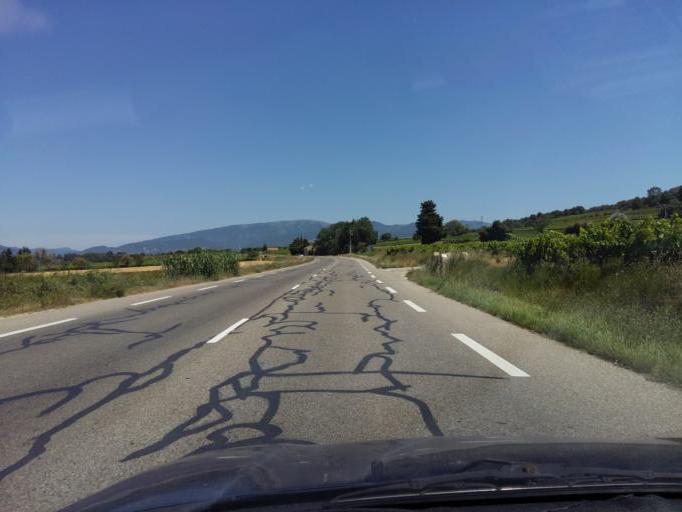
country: FR
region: Provence-Alpes-Cote d'Azur
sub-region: Departement du Vaucluse
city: Valreas
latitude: 44.3553
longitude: 4.9662
